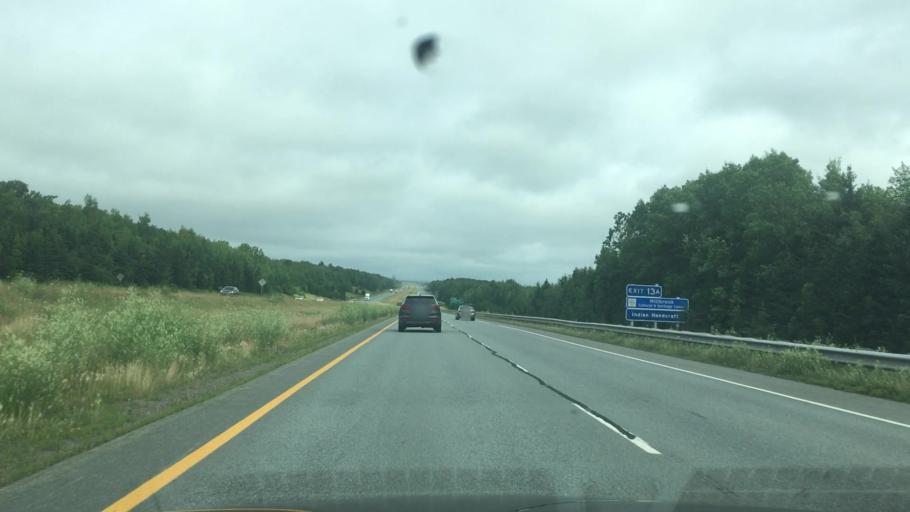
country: CA
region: Nova Scotia
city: Truro
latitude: 45.3061
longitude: -63.3037
